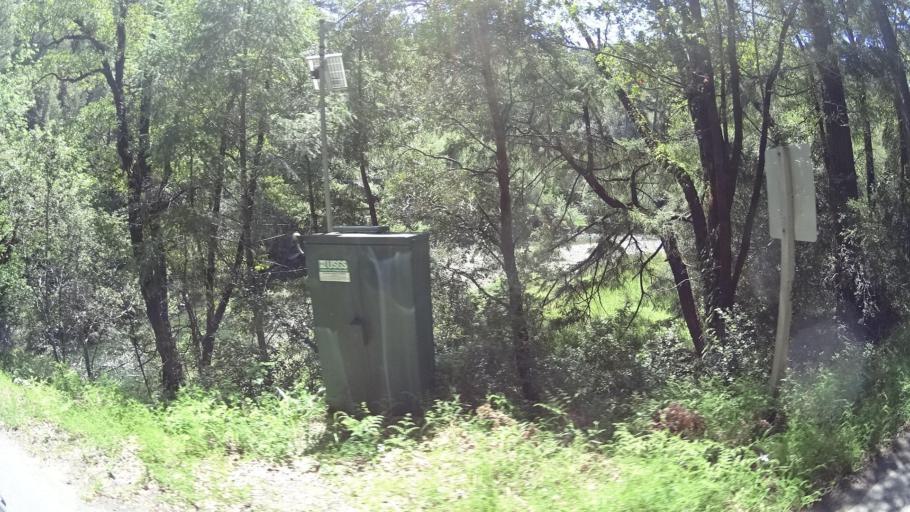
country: US
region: California
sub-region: Humboldt County
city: Redway
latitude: 40.1394
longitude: -123.9919
